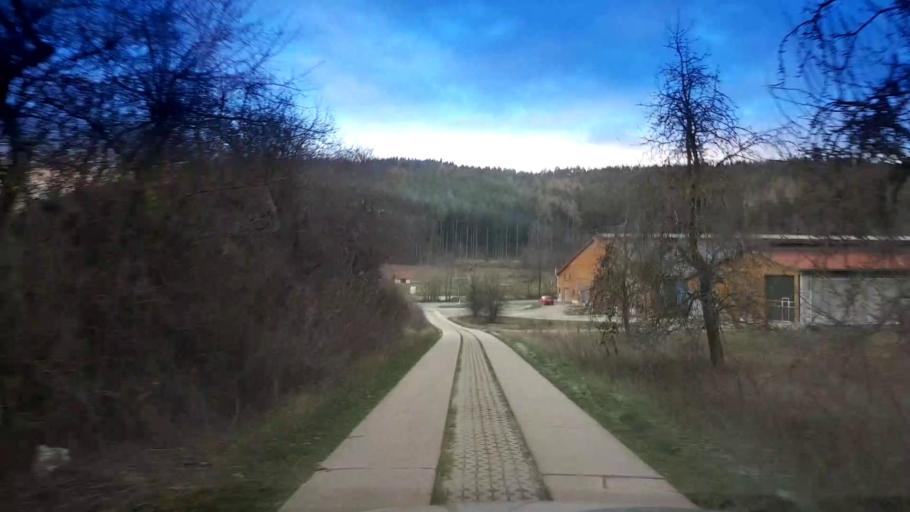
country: DE
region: Bavaria
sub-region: Upper Franconia
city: Schesslitz
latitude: 50.0052
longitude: 11.0697
